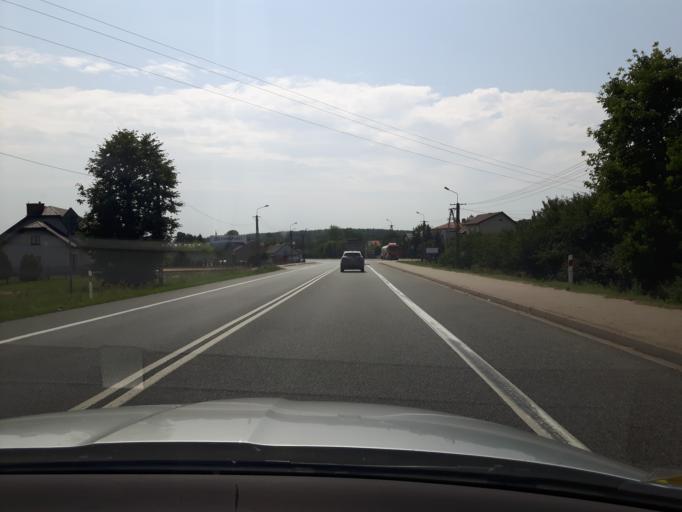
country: PL
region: Masovian Voivodeship
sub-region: Powiat mlawski
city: Mlawa
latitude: 53.1664
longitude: 20.4156
